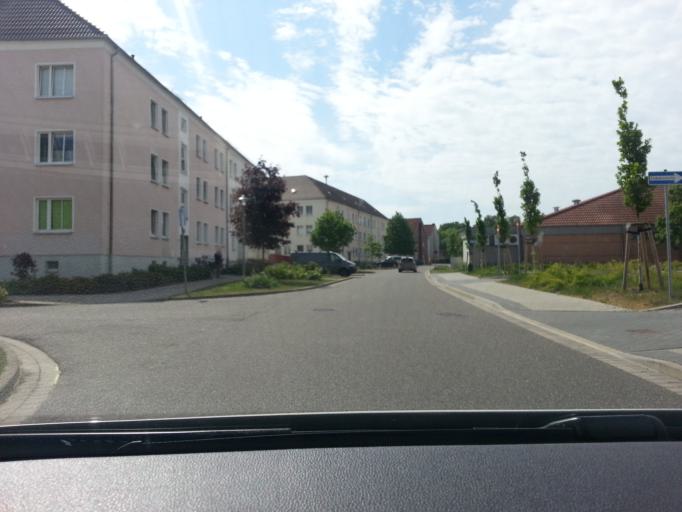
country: DE
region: Mecklenburg-Vorpommern
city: Torgelow
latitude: 53.6352
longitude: 14.0180
